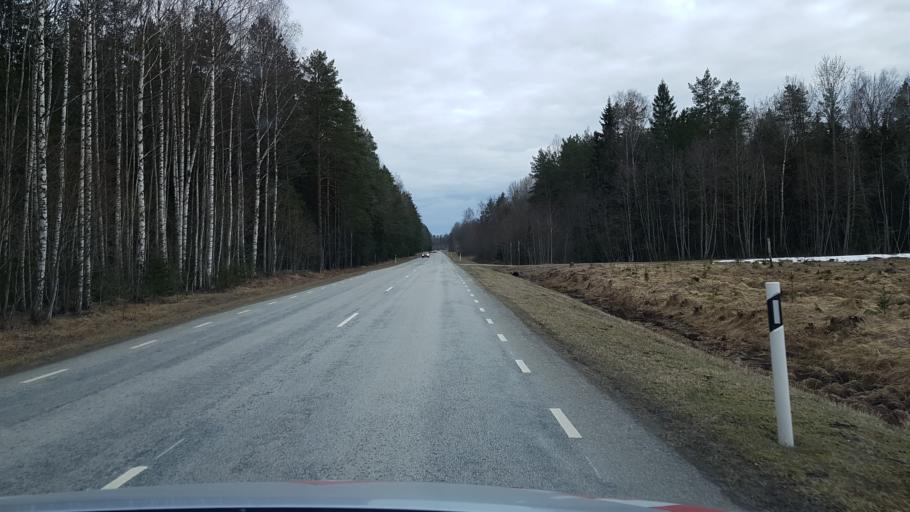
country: EE
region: Ida-Virumaa
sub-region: Toila vald
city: Toila
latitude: 59.3824
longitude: 27.5064
